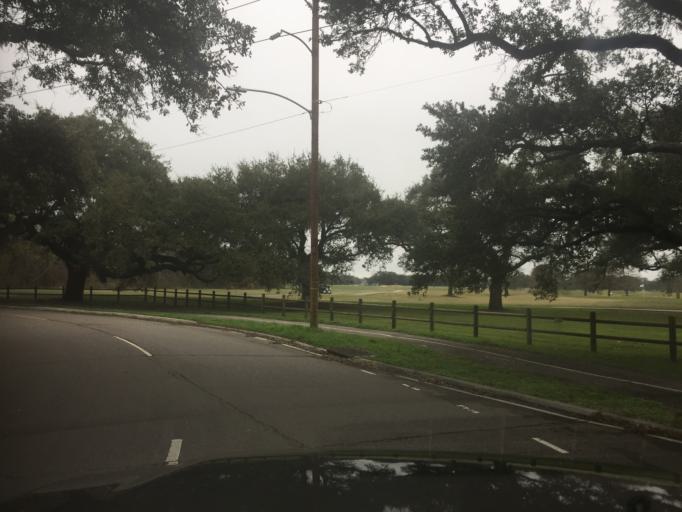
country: US
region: Louisiana
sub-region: Orleans Parish
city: New Orleans
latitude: 30.0016
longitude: -90.0923
